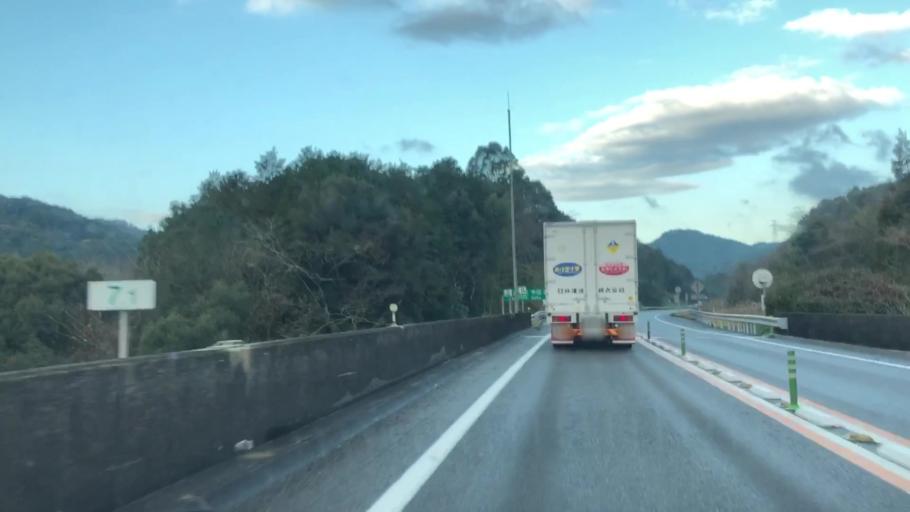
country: JP
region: Saga Prefecture
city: Ureshinomachi-shimojuku
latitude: 33.1567
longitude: 129.9184
